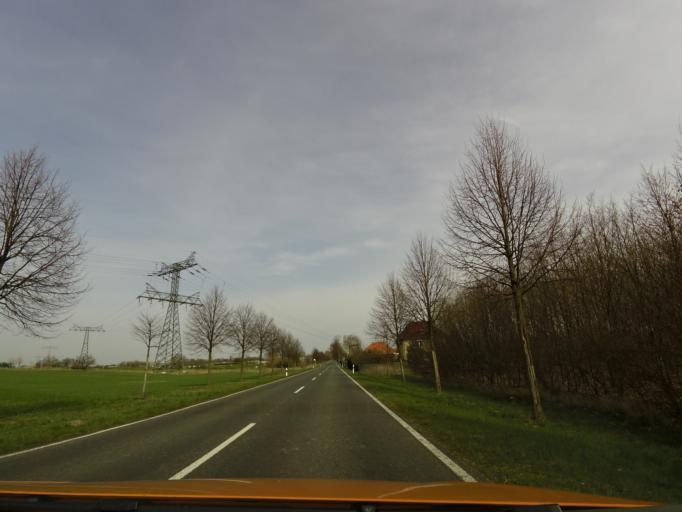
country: DE
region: Brandenburg
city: Ludwigsfelde
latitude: 52.3439
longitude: 13.2623
